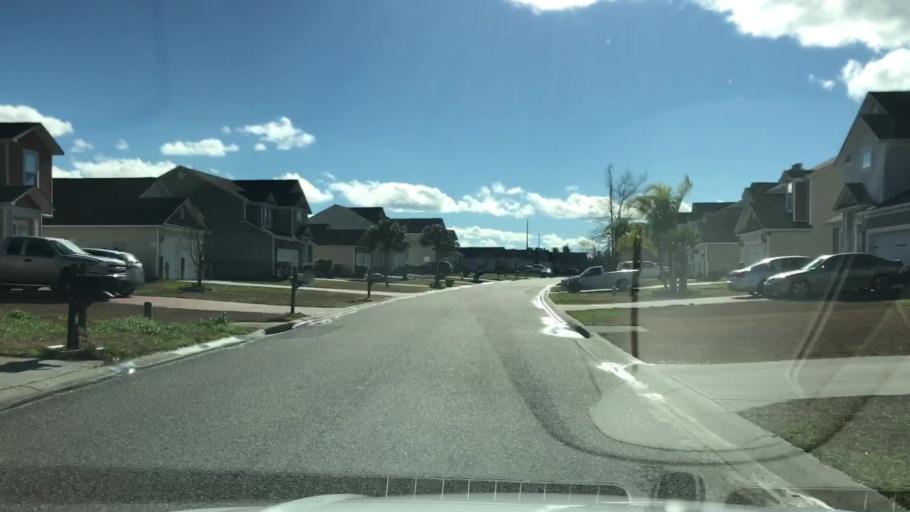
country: US
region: South Carolina
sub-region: Dorchester County
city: Summerville
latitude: 33.0909
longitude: -80.1973
